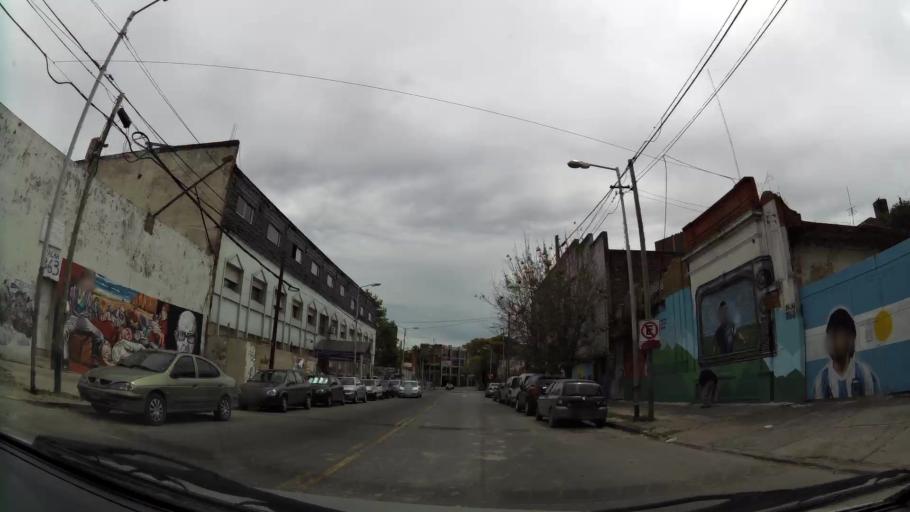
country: AR
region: Buenos Aires
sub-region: Partido de Avellaneda
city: Avellaneda
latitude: -34.6616
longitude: -58.3705
